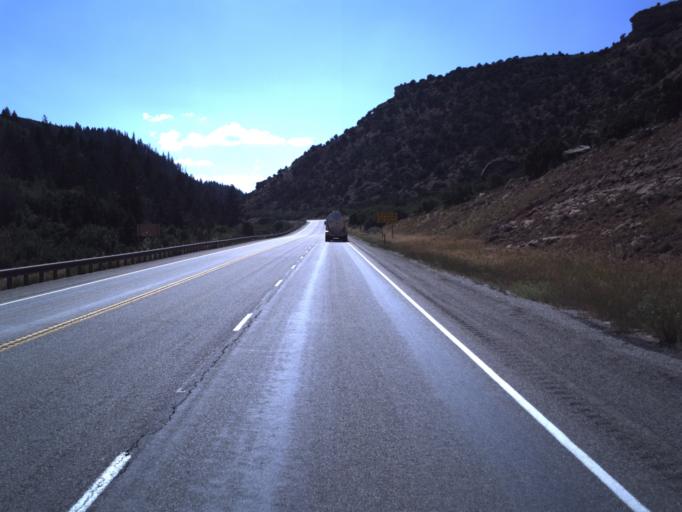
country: US
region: Utah
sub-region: Duchesne County
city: Duchesne
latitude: 40.1999
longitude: -110.9110
